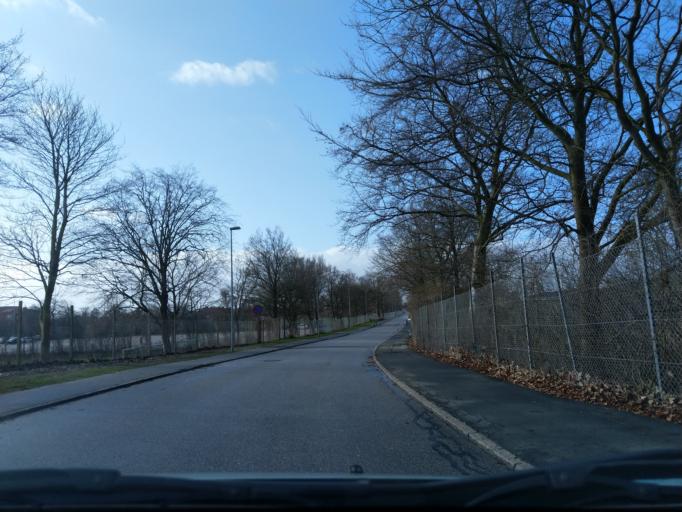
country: DK
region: Zealand
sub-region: Naestved Kommune
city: Naestved
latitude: 55.2229
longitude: 11.7686
